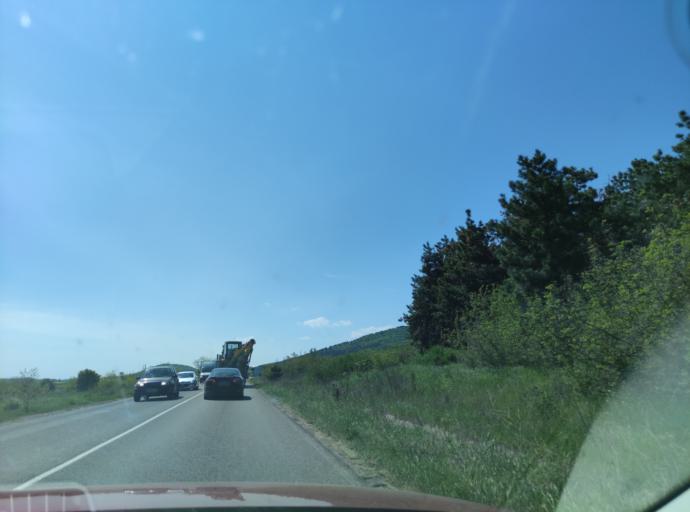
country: BG
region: Stara Zagora
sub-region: Obshtina Stara Zagora
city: Stara Zagora
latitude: 42.3765
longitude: 25.5590
